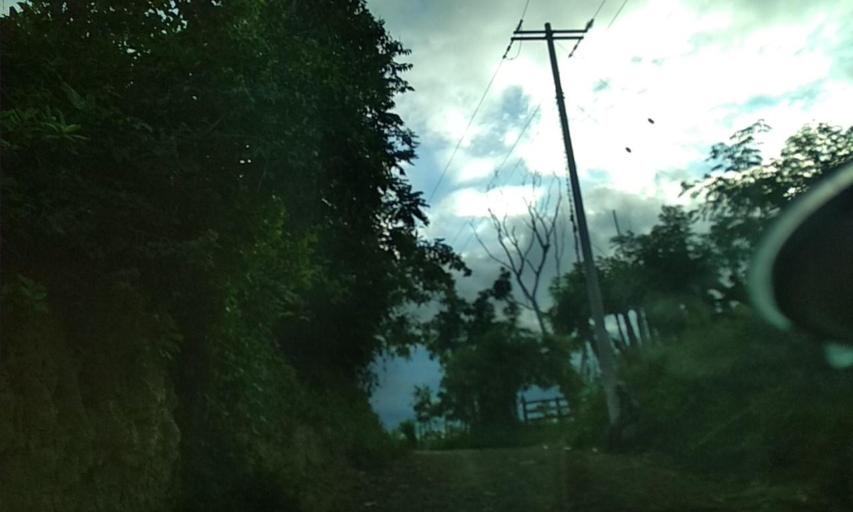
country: MX
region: Veracruz
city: Cazones de Herrera
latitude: 20.6399
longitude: -97.3402
